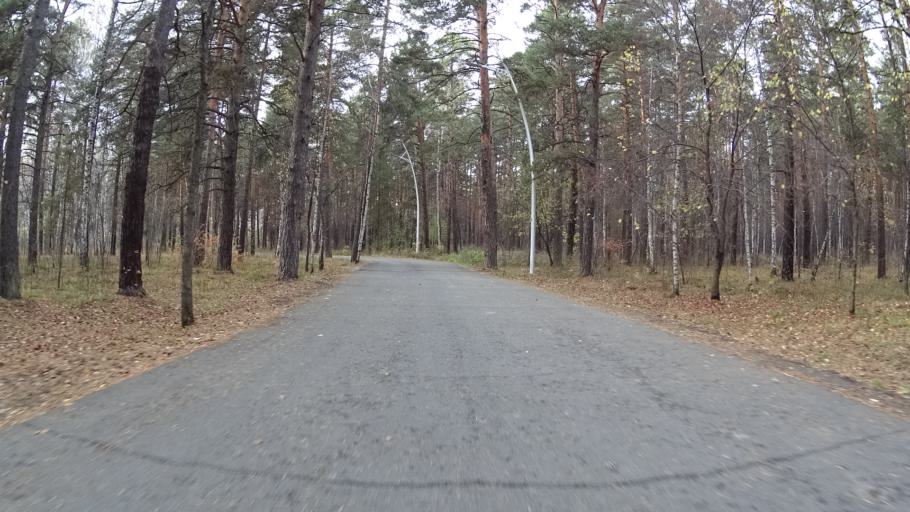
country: RU
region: Chelyabinsk
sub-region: Gorod Chelyabinsk
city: Chelyabinsk
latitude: 55.1394
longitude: 61.3511
